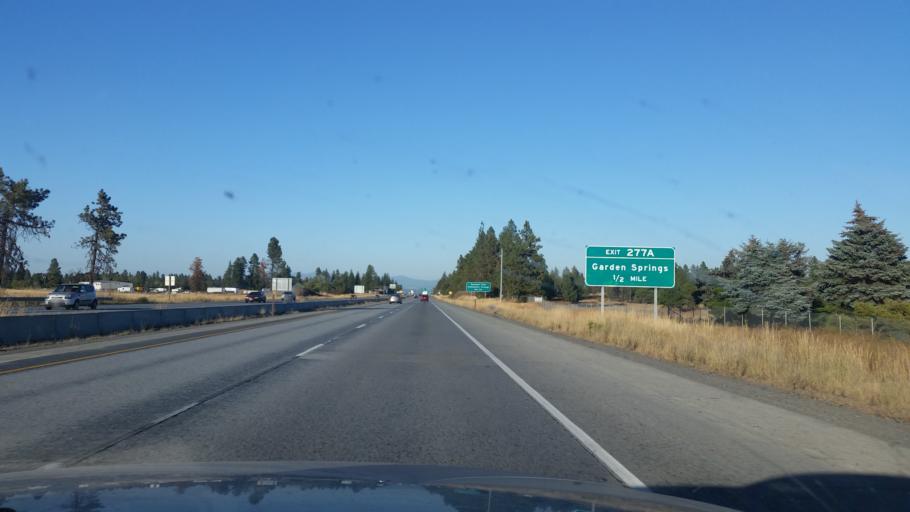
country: US
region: Washington
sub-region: Spokane County
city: Spokane
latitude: 47.6234
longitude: -117.4967
